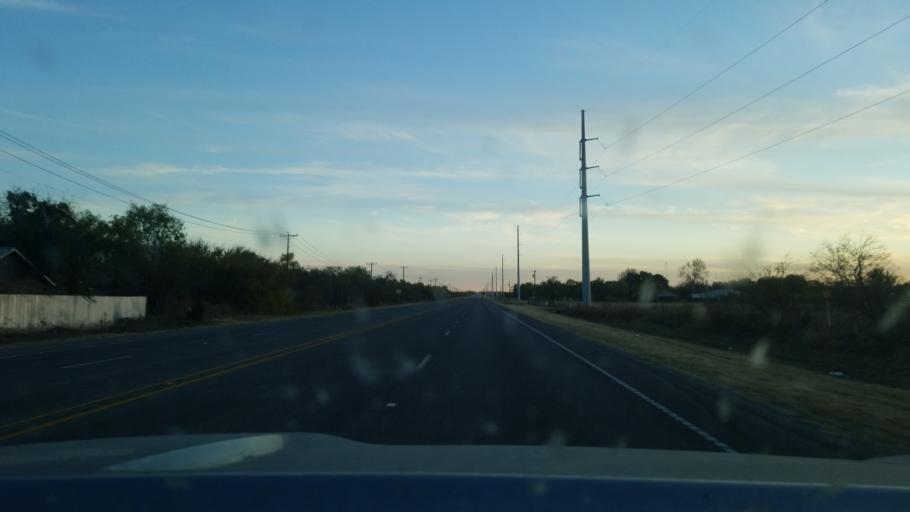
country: US
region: Texas
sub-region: Stephens County
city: Breckenridge
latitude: 32.7389
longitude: -98.9027
